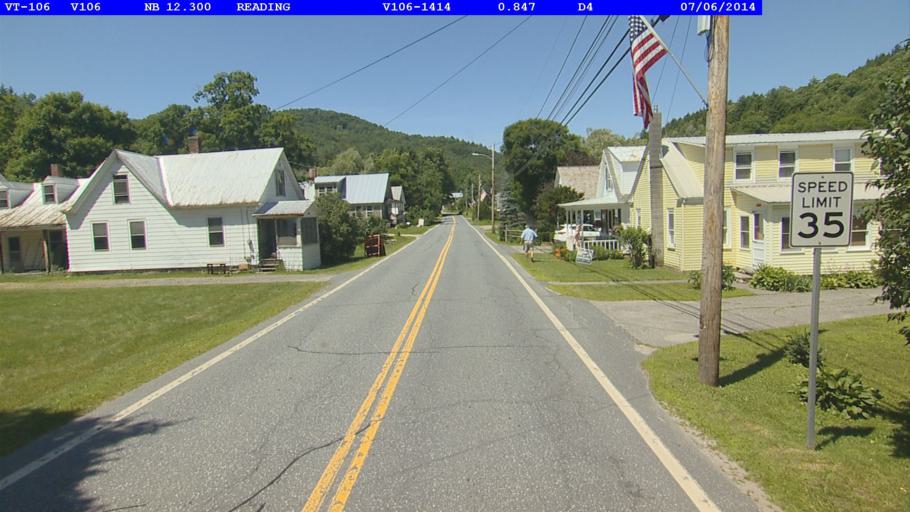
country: US
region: Vermont
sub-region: Windsor County
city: Windsor
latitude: 43.4563
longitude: -72.5371
